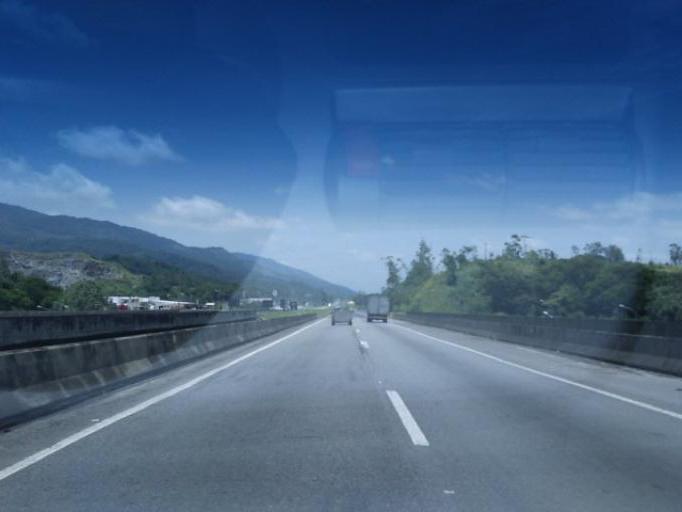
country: BR
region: Sao Paulo
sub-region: Miracatu
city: Miracatu
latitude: -24.2706
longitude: -47.4015
